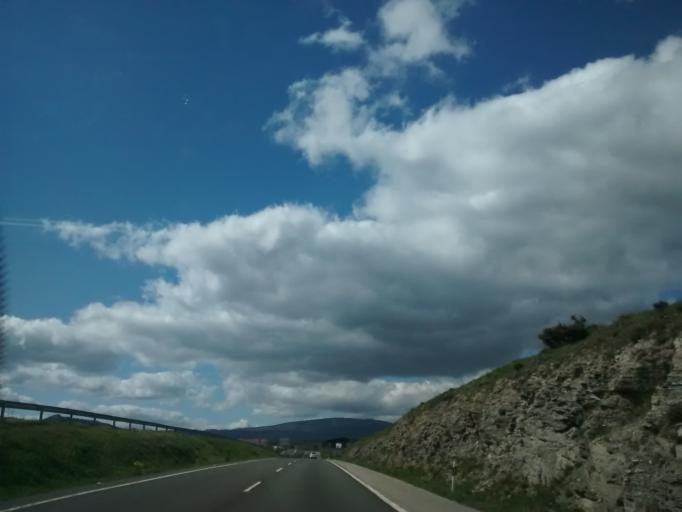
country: ES
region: Basque Country
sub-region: Provincia de Alava
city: Gasteiz / Vitoria
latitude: 42.9136
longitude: -2.7208
